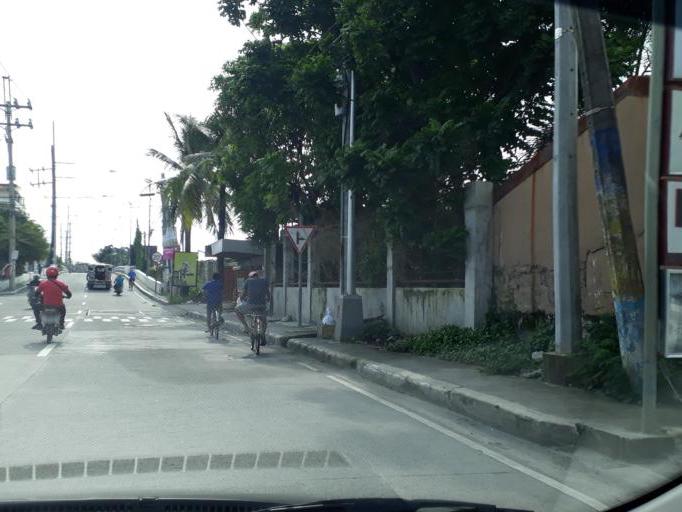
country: PH
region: Calabarzon
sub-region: Province of Rizal
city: Navotas
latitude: 14.6709
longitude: 120.9543
